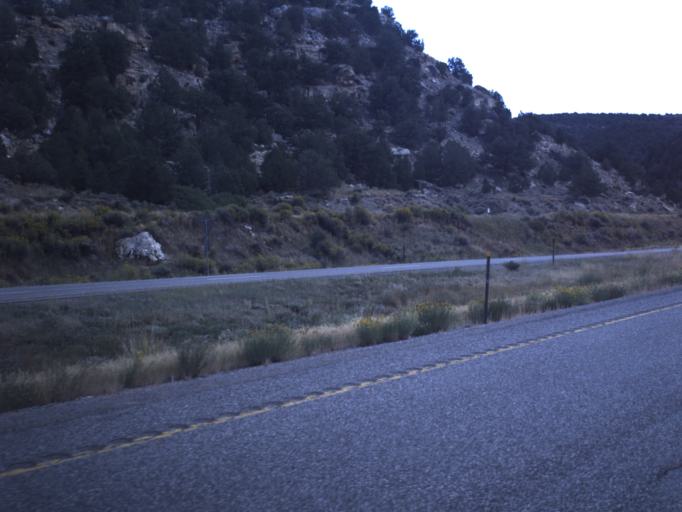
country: US
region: Utah
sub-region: Sevier County
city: Salina
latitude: 38.8477
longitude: -111.5405
